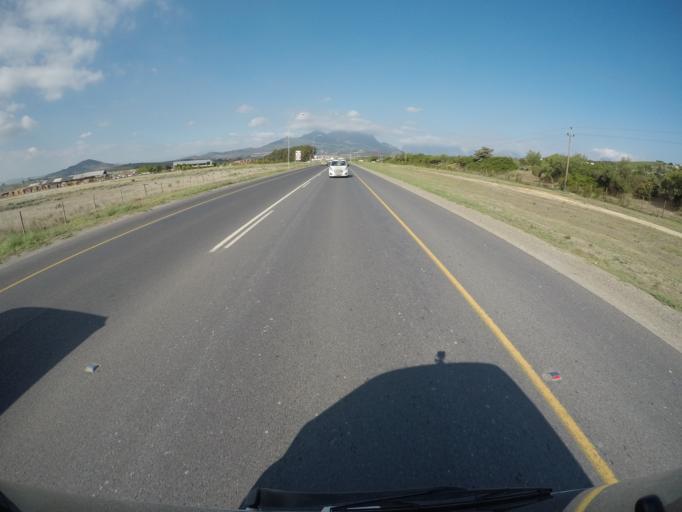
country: ZA
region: Western Cape
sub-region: Cape Winelands District Municipality
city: Stellenbosch
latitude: -33.8780
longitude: 18.8004
